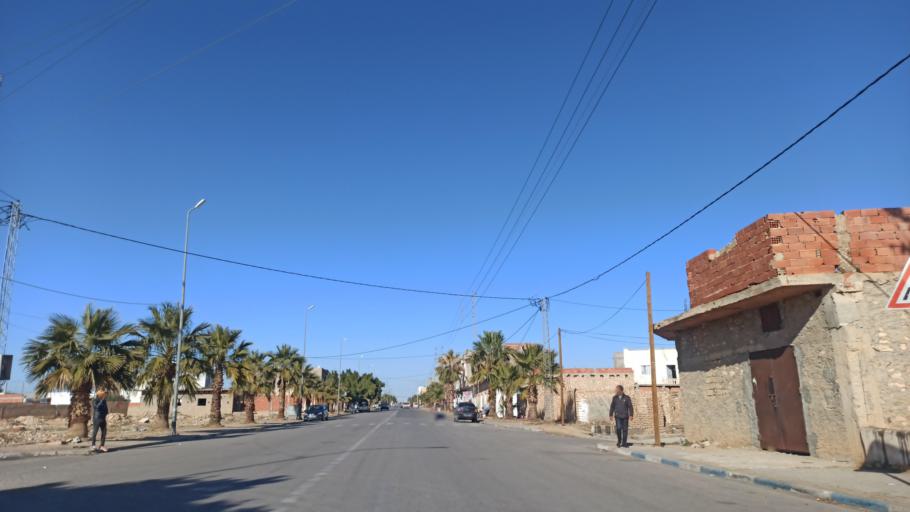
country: TN
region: Sidi Bu Zayd
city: Jilma
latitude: 35.2748
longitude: 9.4190
